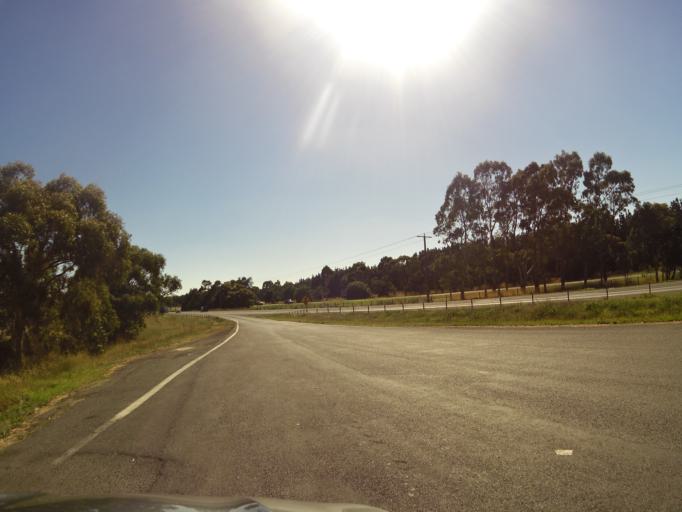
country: AU
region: Victoria
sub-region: Hume
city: Craigieburn
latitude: -37.4956
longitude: 144.9592
